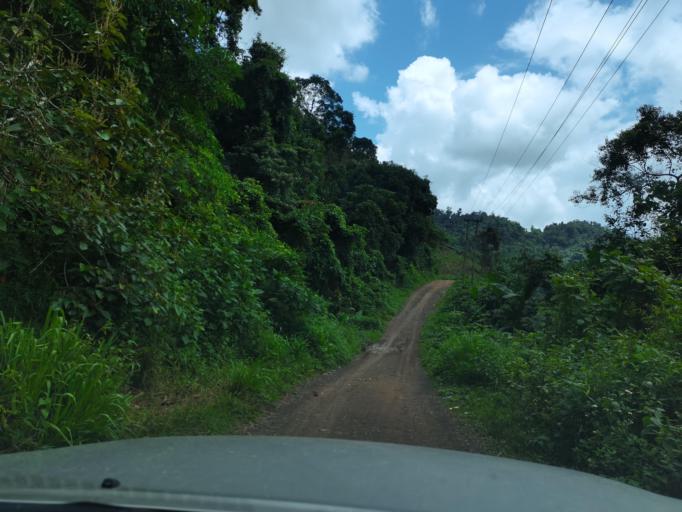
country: LA
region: Loungnamtha
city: Muang Long
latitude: 20.7473
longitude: 101.0188
